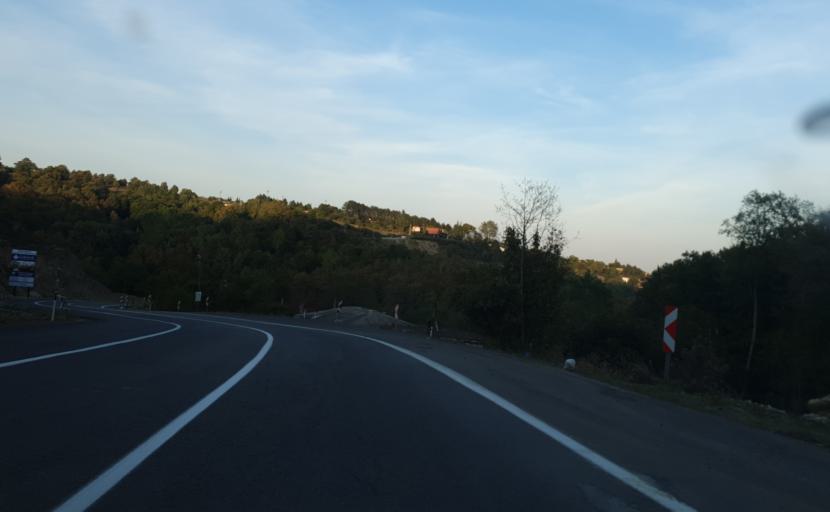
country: TR
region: Kirklareli
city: Sergen
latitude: 41.8190
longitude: 27.7502
